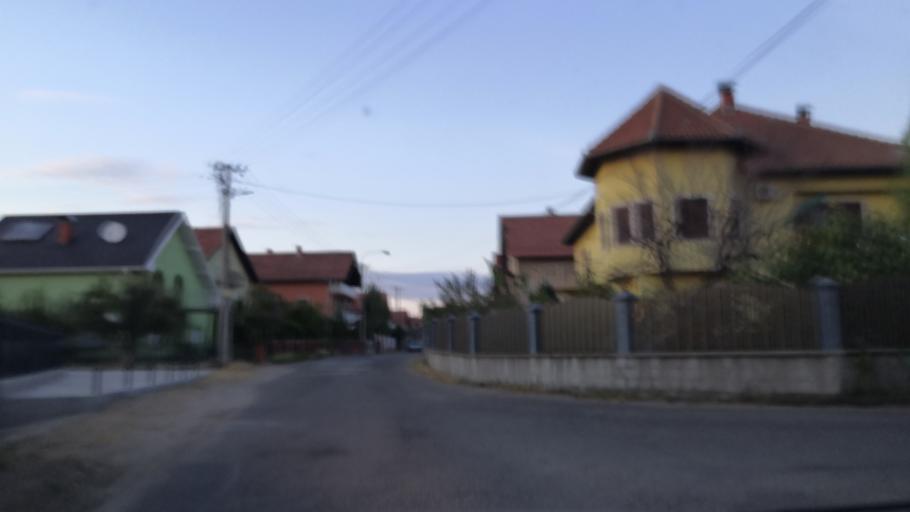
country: RS
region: Central Serbia
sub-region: Borski Okrug
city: Negotin
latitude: 44.2394
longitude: 22.5290
